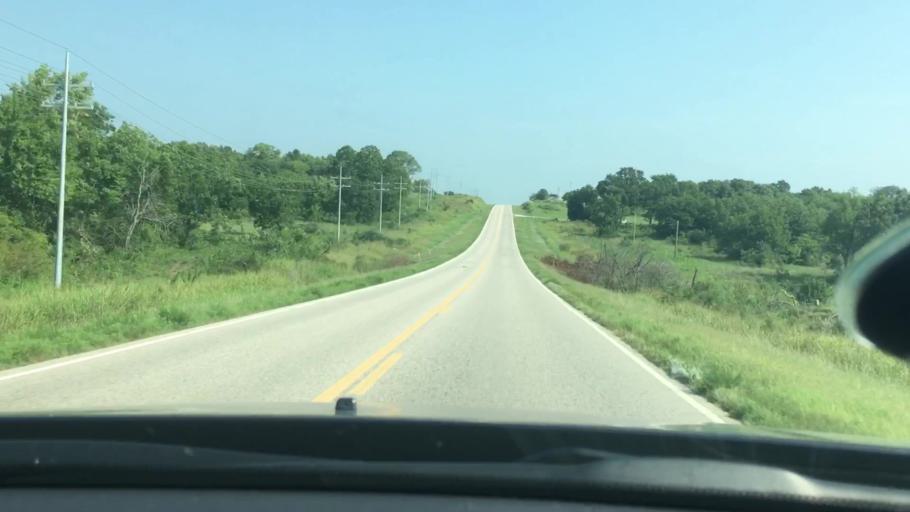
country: US
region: Oklahoma
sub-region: Pontotoc County
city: Ada
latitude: 34.6266
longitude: -96.6348
